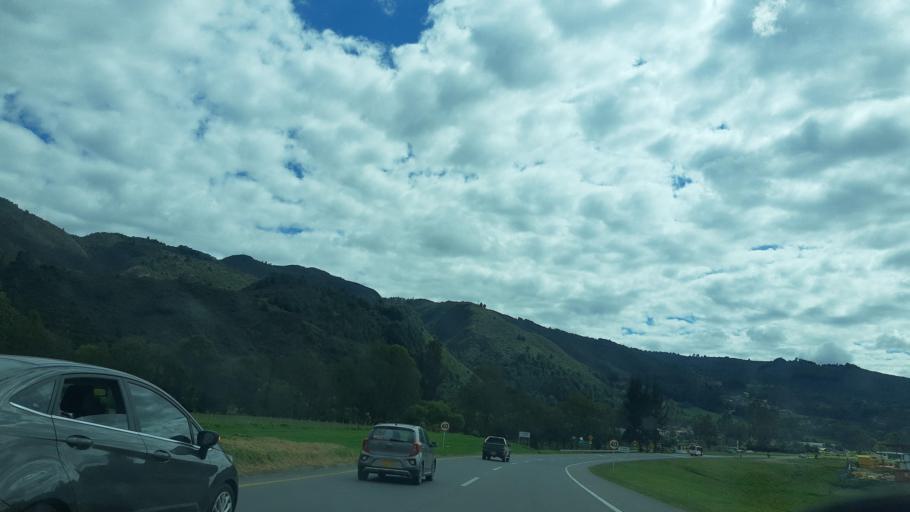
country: CO
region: Cundinamarca
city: Gachancipa
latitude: 4.9874
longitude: -73.8803
